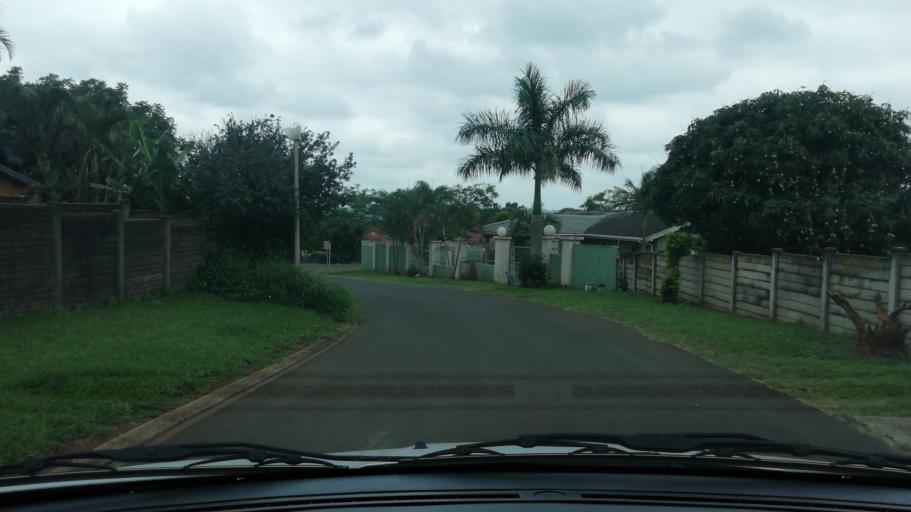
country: ZA
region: KwaZulu-Natal
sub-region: uThungulu District Municipality
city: Empangeni
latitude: -28.7616
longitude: 31.8824
